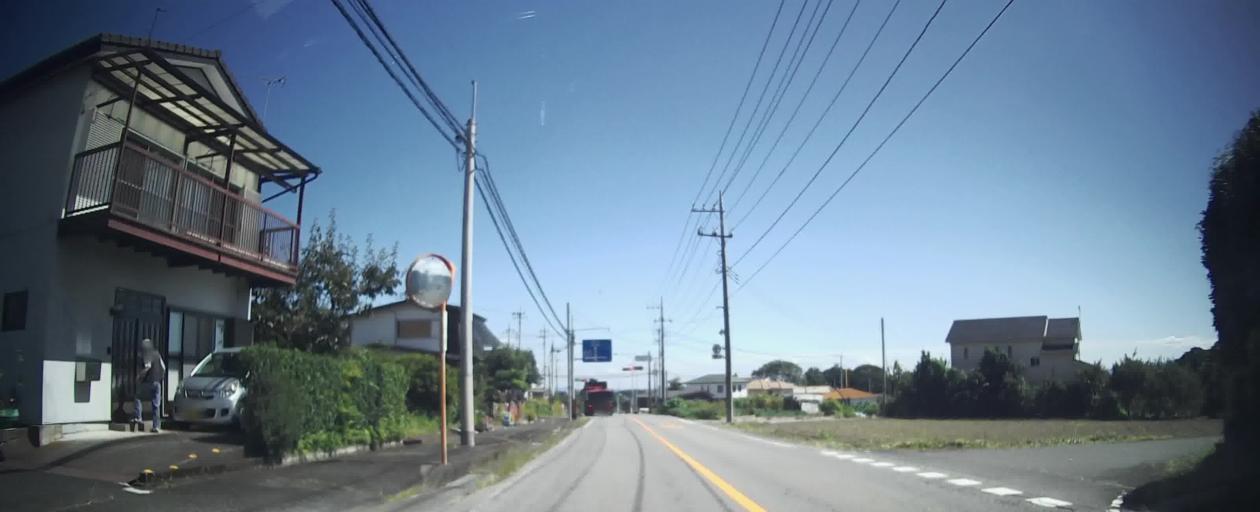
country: JP
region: Gunma
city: Kanekomachi
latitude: 36.4089
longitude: 138.9513
